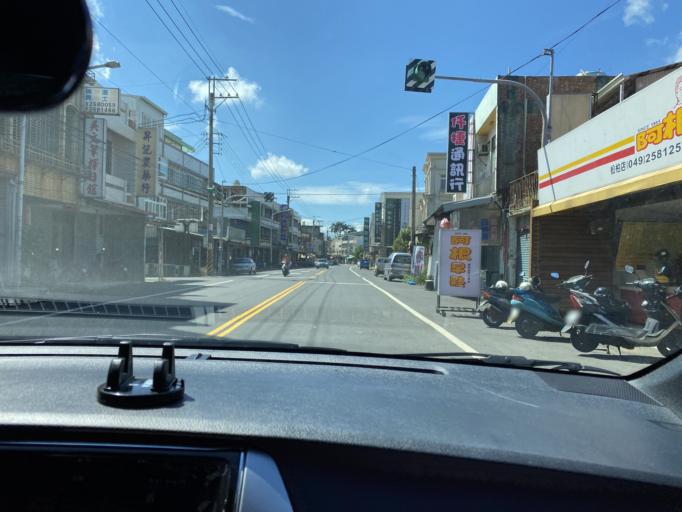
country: TW
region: Taiwan
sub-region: Nantou
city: Nantou
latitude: 23.8369
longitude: 120.6339
